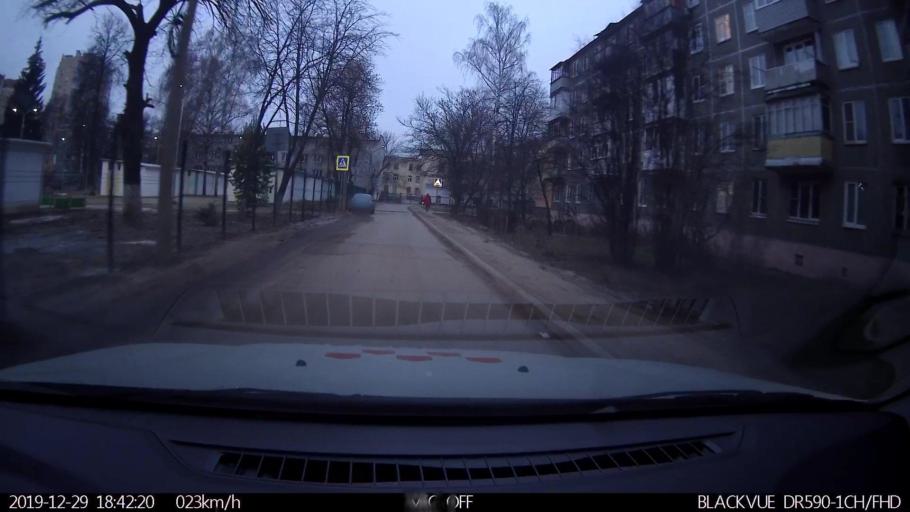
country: RU
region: Nizjnij Novgorod
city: Neklyudovo
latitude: 56.3437
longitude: 43.8679
